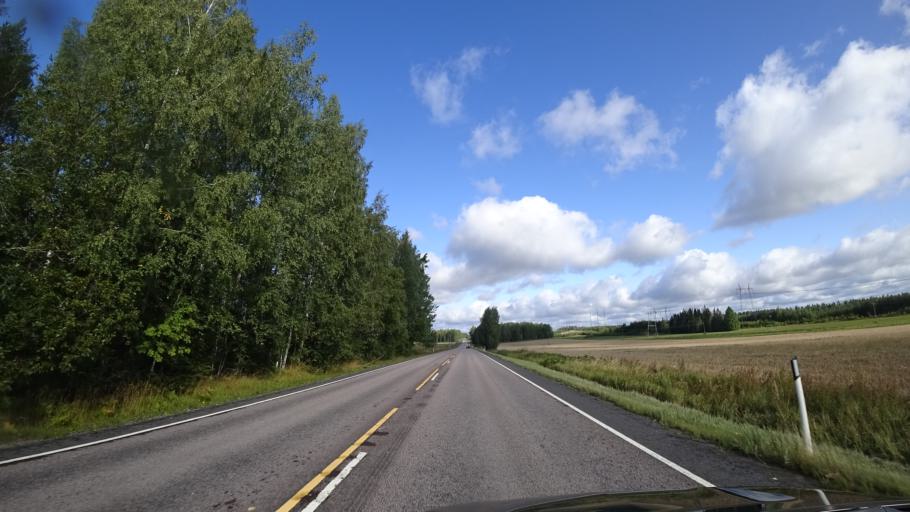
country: FI
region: Uusimaa
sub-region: Helsinki
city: Tuusula
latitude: 60.4988
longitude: 24.9356
